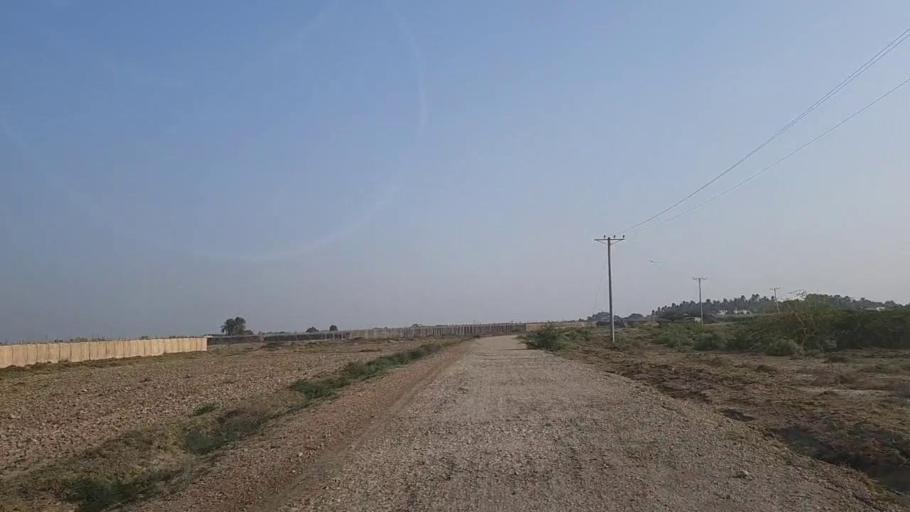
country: PK
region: Sindh
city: Keti Bandar
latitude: 24.1696
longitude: 67.6253
